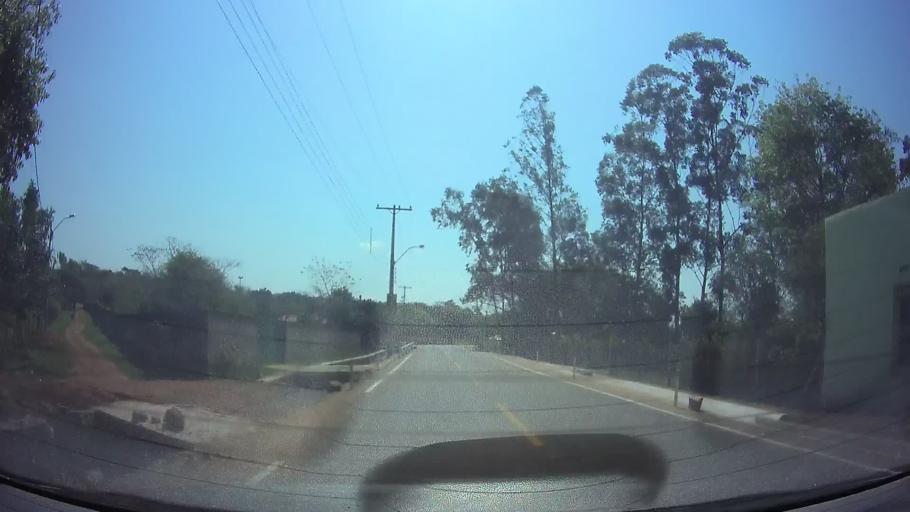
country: PY
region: Central
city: Limpio
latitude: -25.2449
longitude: -57.4925
